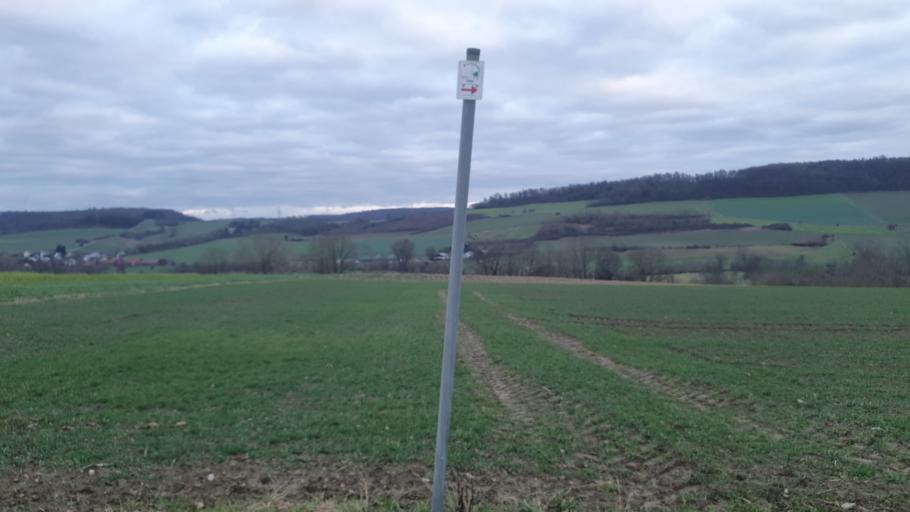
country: DE
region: North Rhine-Westphalia
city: Brakel
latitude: 51.6979
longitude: 9.2256
